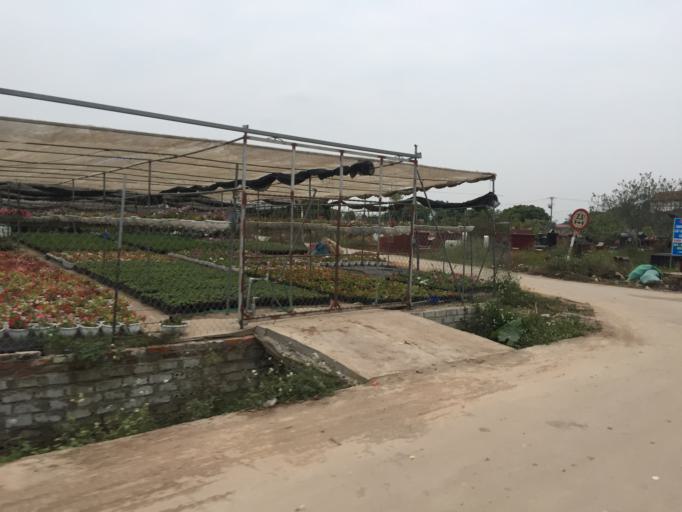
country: VN
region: Hung Yen
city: Van Giang
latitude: 20.9692
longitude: 105.9135
